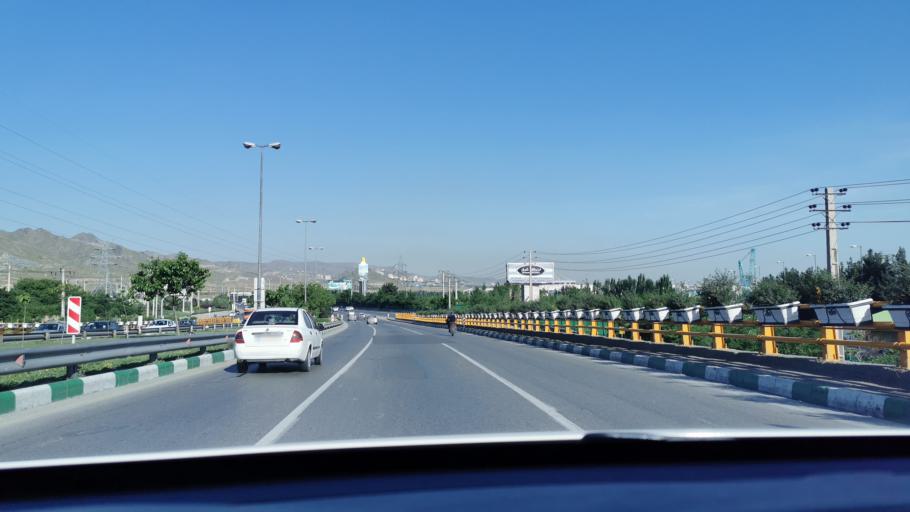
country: IR
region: Razavi Khorasan
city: Mashhad
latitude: 36.2565
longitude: 59.5972
